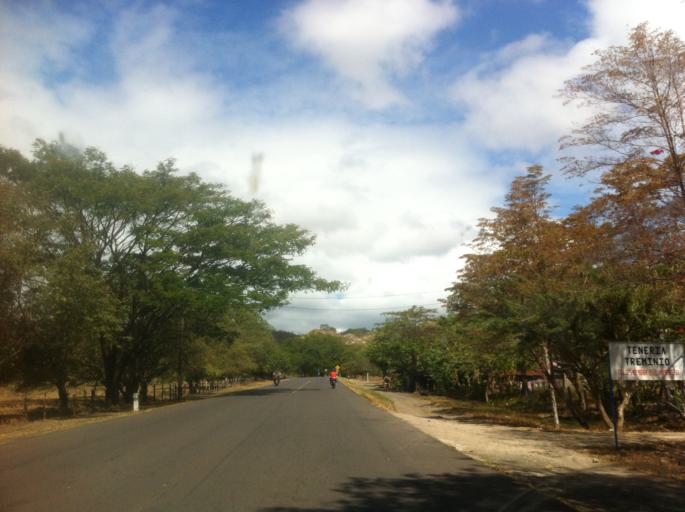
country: NI
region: Chontales
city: Acoyapa
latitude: 12.0373
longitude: -85.2671
